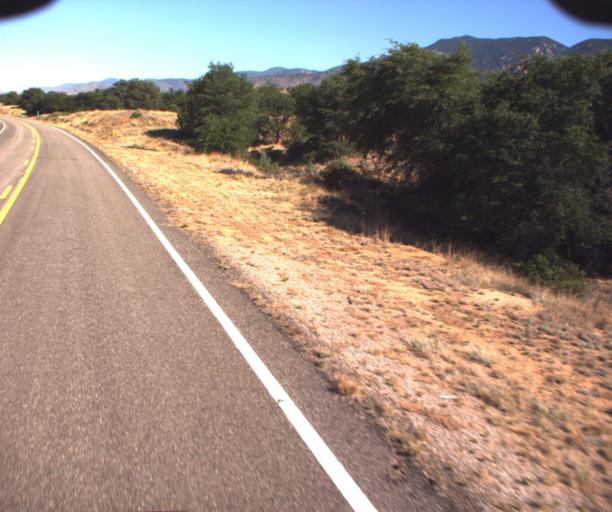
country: US
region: Arizona
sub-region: Graham County
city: Swift Trail Junction
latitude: 32.5958
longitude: -109.8595
